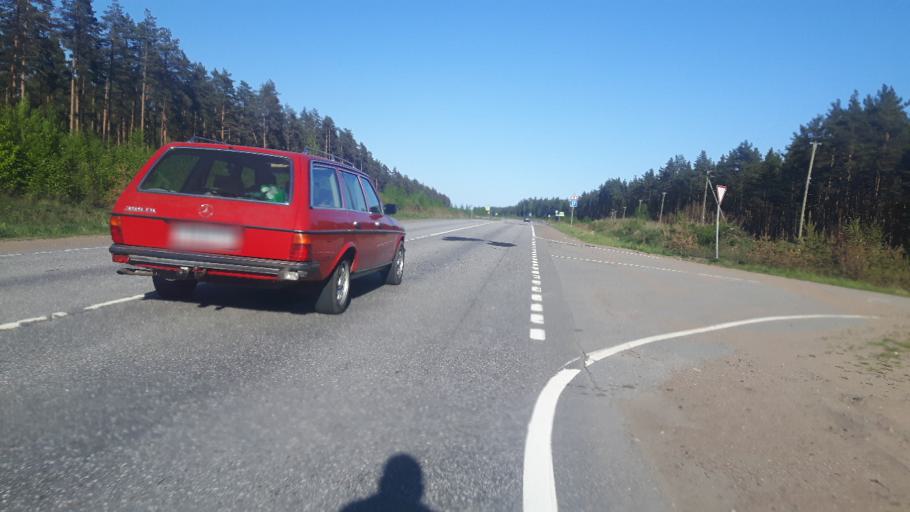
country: RU
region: Leningrad
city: Lebyazh'ye
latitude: 60.1687
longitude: 29.2139
